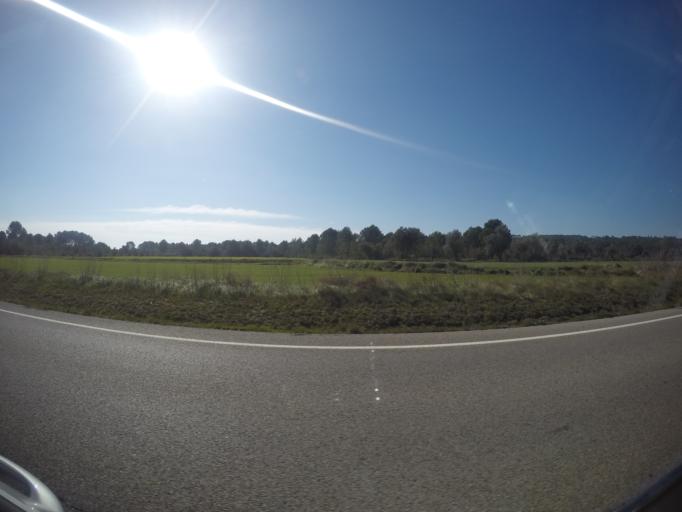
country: ES
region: Catalonia
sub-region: Provincia de Girona
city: Ventallo
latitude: 42.1418
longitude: 3.0482
